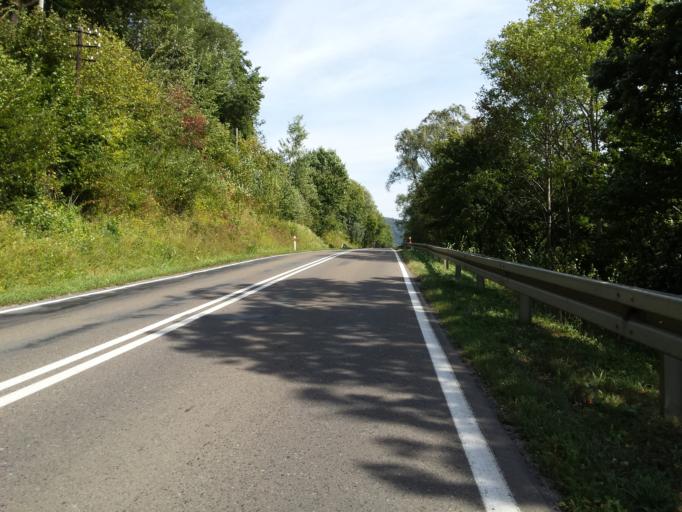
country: PL
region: Subcarpathian Voivodeship
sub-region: Powiat leski
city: Lesko
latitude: 49.4309
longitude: 22.3334
